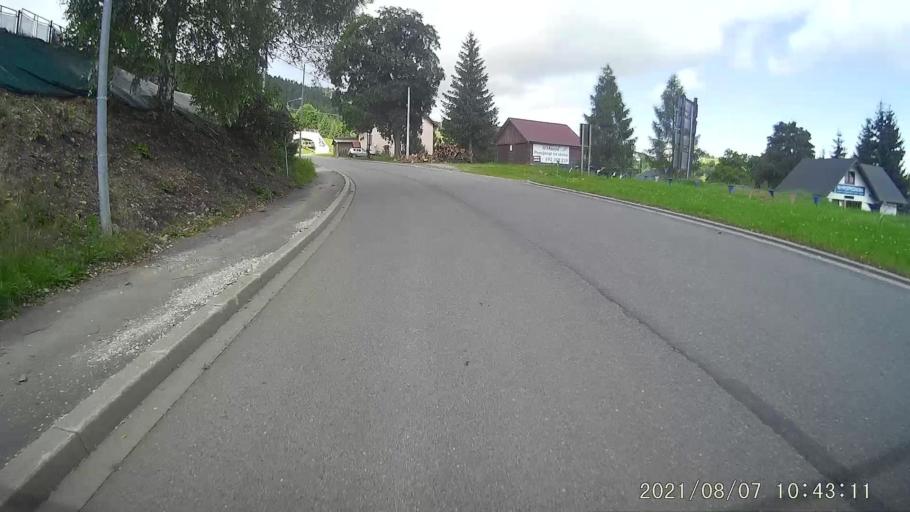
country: PL
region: Lower Silesian Voivodeship
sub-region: Powiat klodzki
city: Duszniki-Zdroj
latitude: 50.3289
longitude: 16.3943
